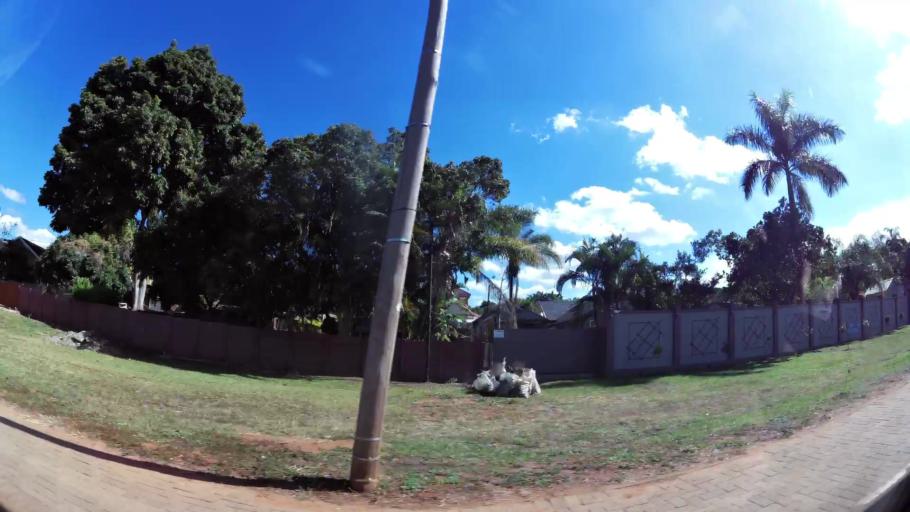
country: ZA
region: Limpopo
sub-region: Mopani District Municipality
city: Tzaneen
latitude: -23.8152
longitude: 30.1590
